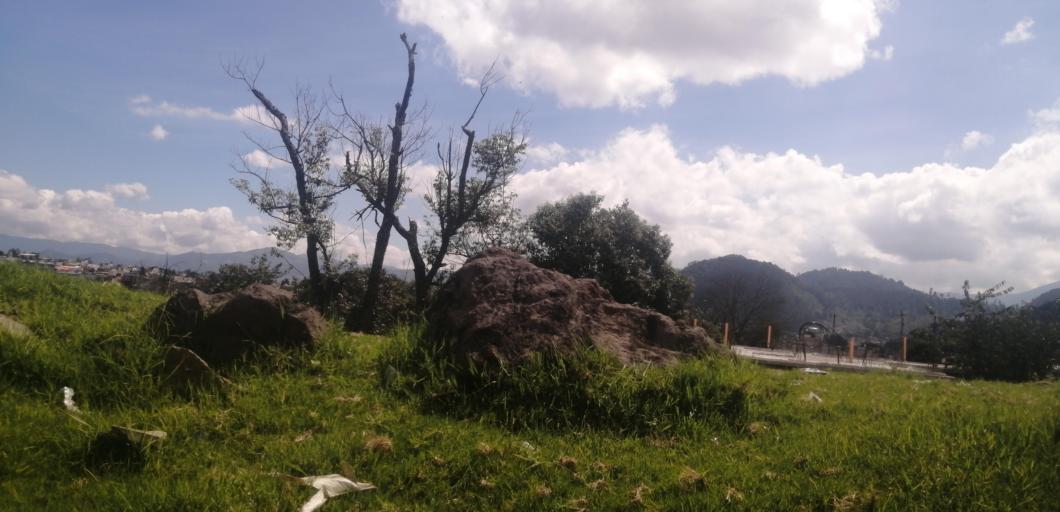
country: GT
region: Quetzaltenango
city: Quetzaltenango
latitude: 14.8342
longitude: -91.5316
